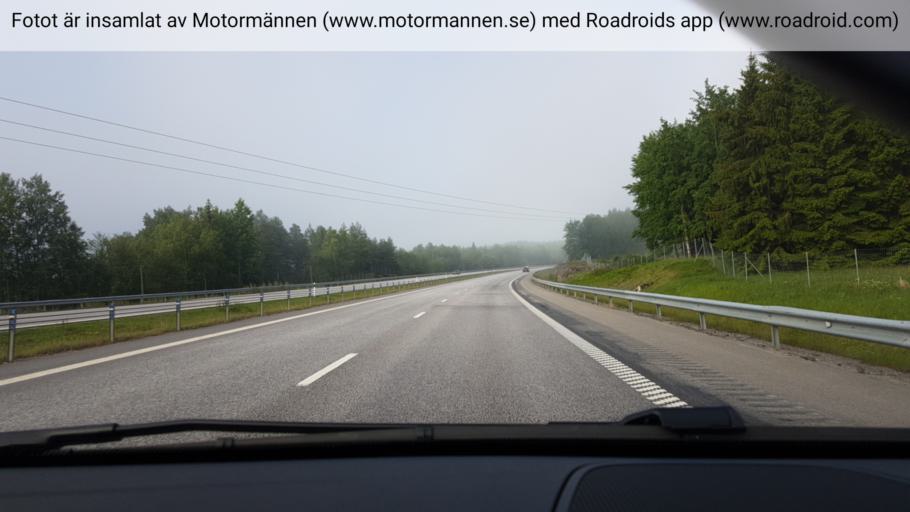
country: SE
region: Soedermanland
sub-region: Nykopings Kommun
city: Nykoping
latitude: 58.8211
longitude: 17.1468
